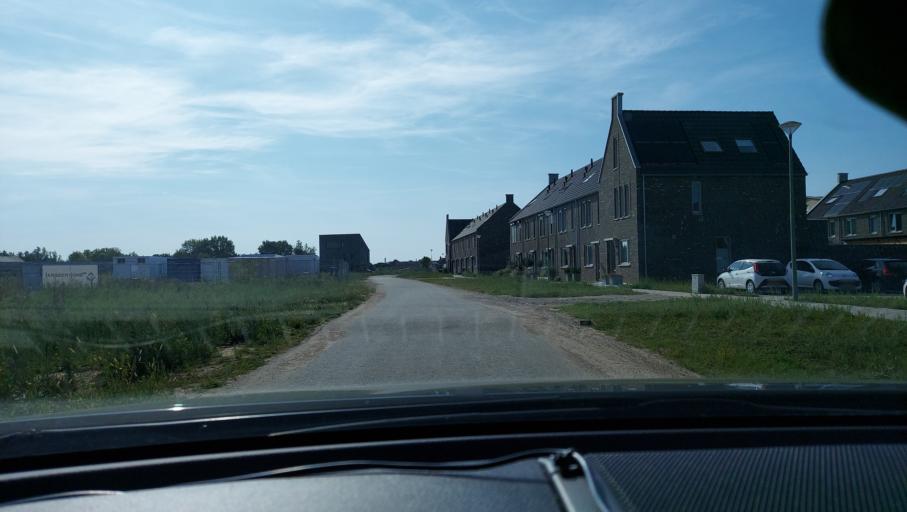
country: NL
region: Limburg
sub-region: Gemeente Roermond
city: Leeuwen
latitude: 51.2045
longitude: 6.0168
